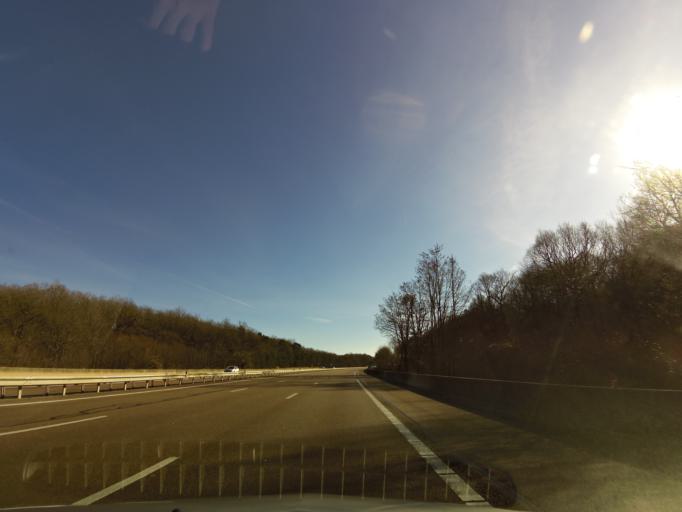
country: FR
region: Bourgogne
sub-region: Departement de l'Yonne
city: Aillant-sur-Tholon
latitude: 47.9221
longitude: 3.2827
